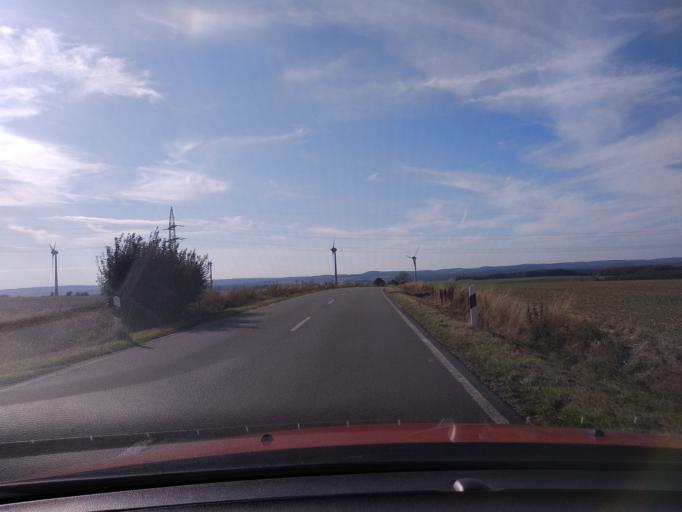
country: DE
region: North Rhine-Westphalia
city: Brakel
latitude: 51.6492
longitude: 9.2030
